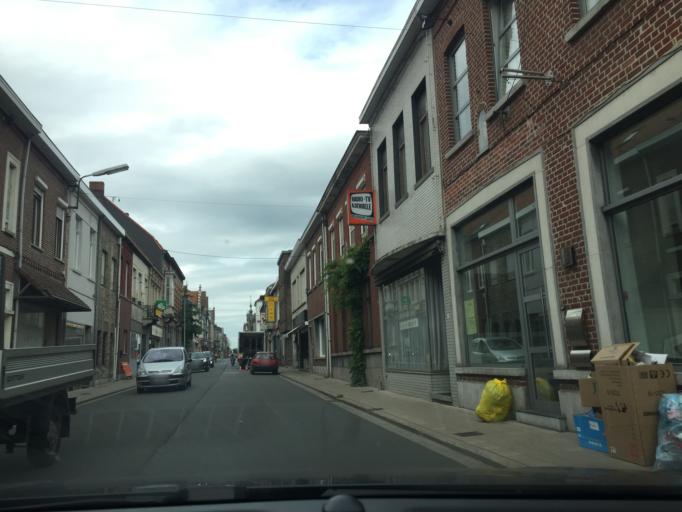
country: BE
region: Flanders
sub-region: Provincie West-Vlaanderen
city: Izegem
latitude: 50.9163
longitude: 3.2122
